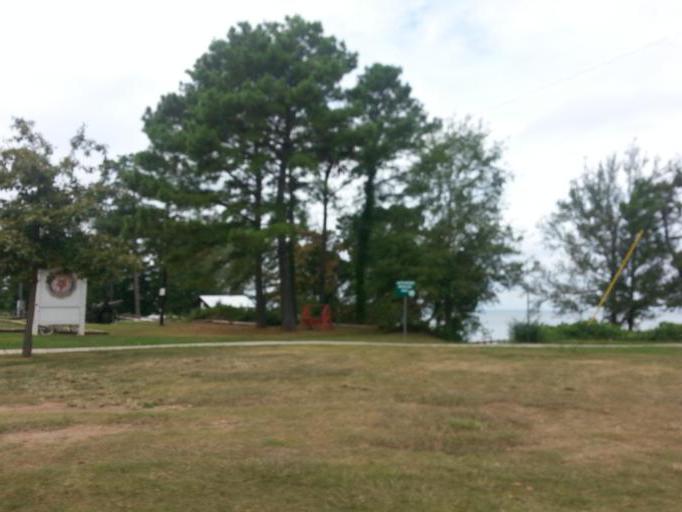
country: US
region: Alabama
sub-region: Baldwin County
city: Fairhope
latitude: 30.5139
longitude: -87.9183
